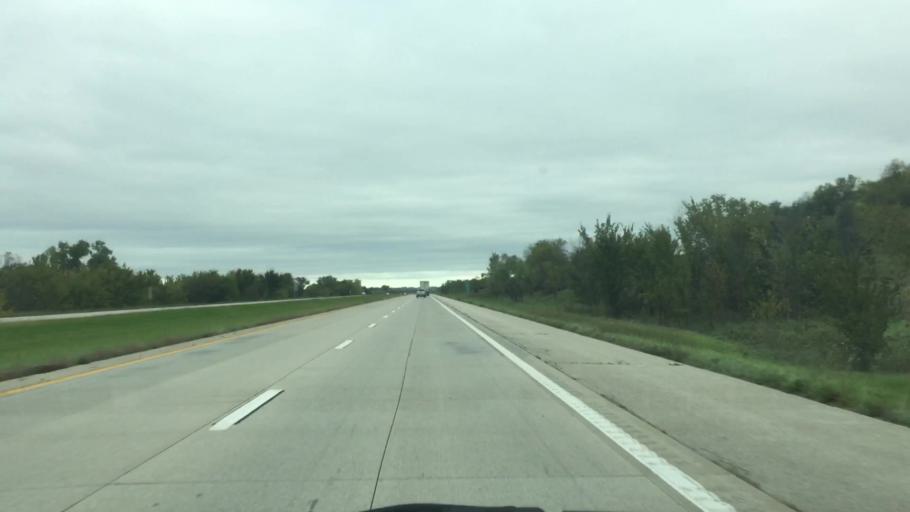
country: US
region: Missouri
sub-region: Daviess County
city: Gallatin
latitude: 39.9852
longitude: -94.0947
